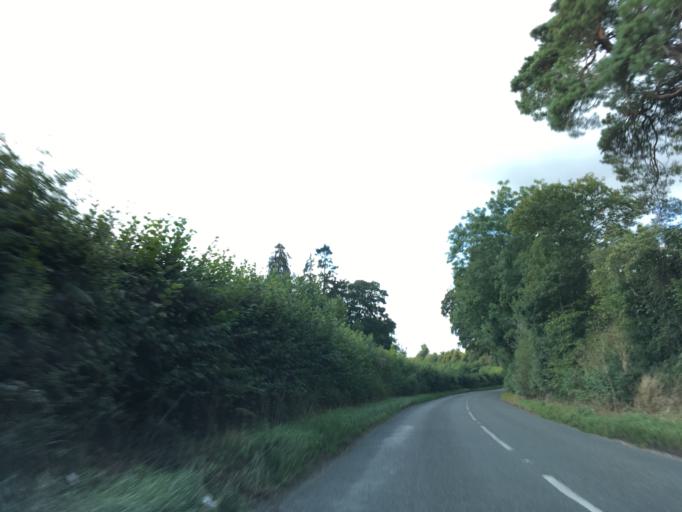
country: GB
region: England
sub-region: Hampshire
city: Overton
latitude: 51.2212
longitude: -1.3608
